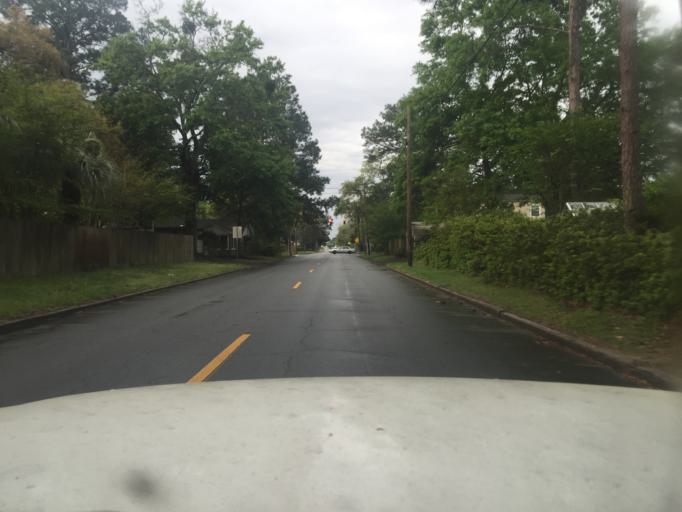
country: US
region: Georgia
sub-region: Chatham County
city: Thunderbolt
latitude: 32.0374
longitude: -81.0935
